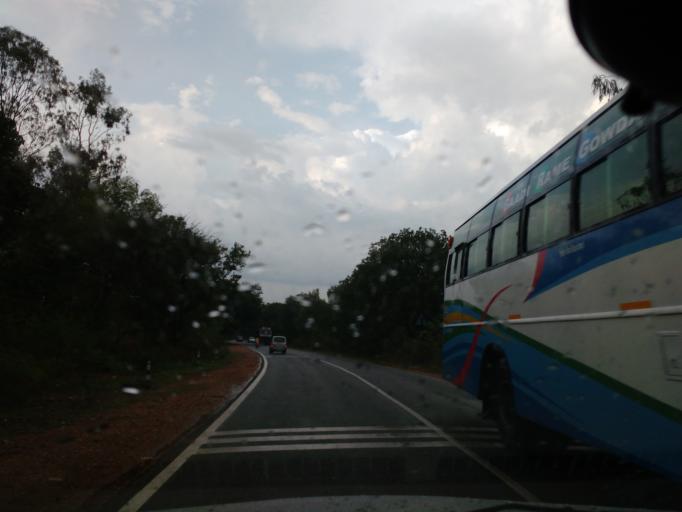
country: IN
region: Karnataka
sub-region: Tumkur
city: Chiknayakanhalli
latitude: 13.3015
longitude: 76.5919
